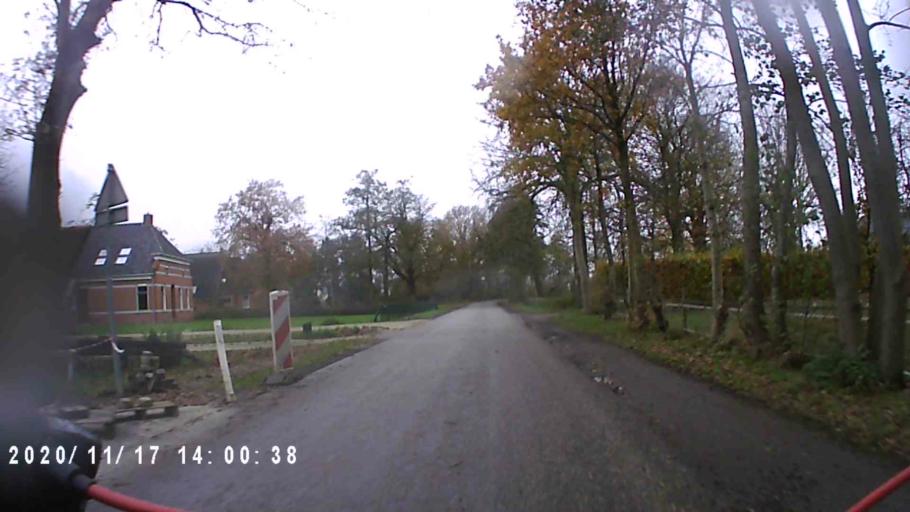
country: NL
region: Groningen
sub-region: Gemeente Zuidhorn
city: Grijpskerk
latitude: 53.2272
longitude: 6.3426
